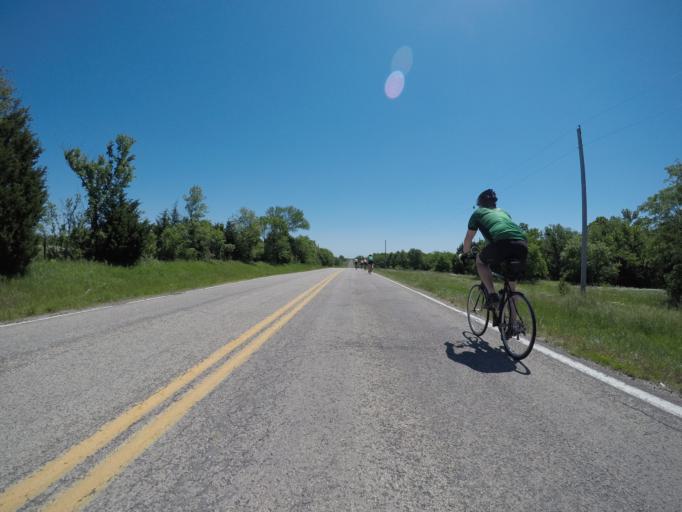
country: US
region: Kansas
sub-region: Shawnee County
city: Auburn
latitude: 38.9064
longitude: -95.9480
